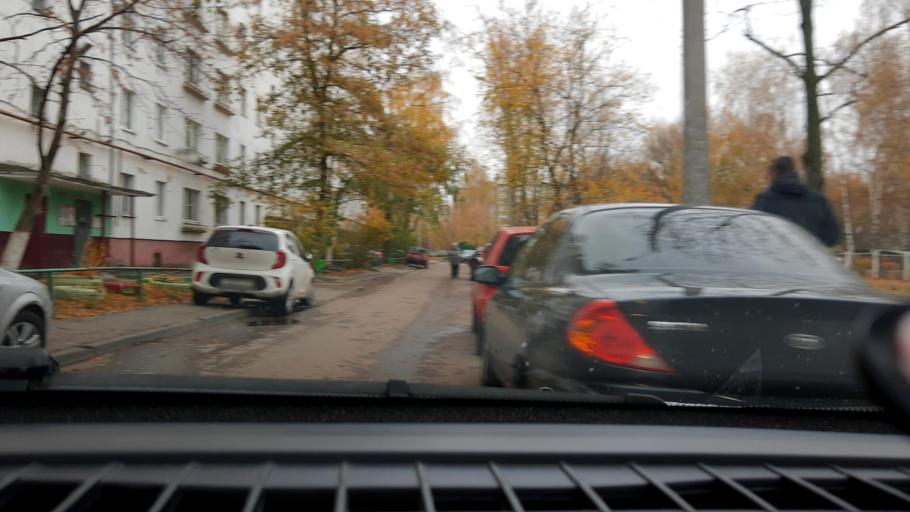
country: RU
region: Nizjnij Novgorod
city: Nizhniy Novgorod
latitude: 56.2616
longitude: 43.8957
